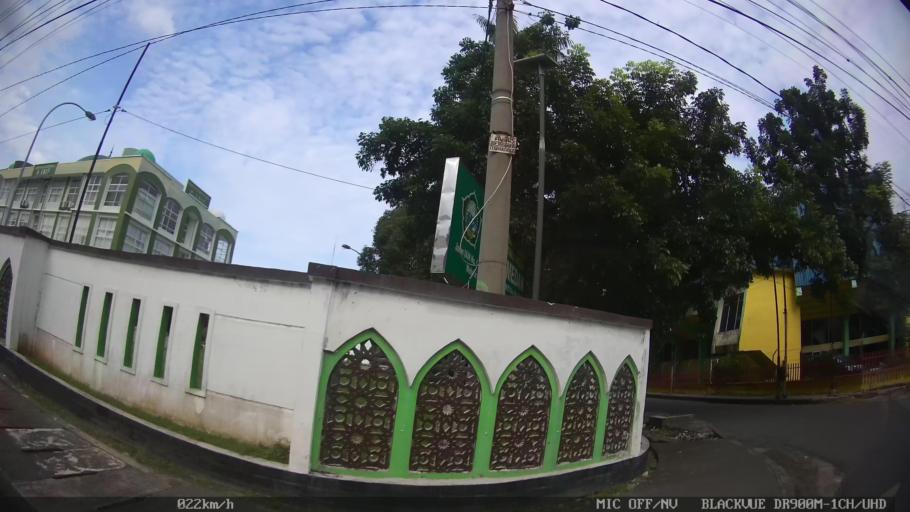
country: ID
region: North Sumatra
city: Medan
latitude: 3.6002
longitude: 98.6810
